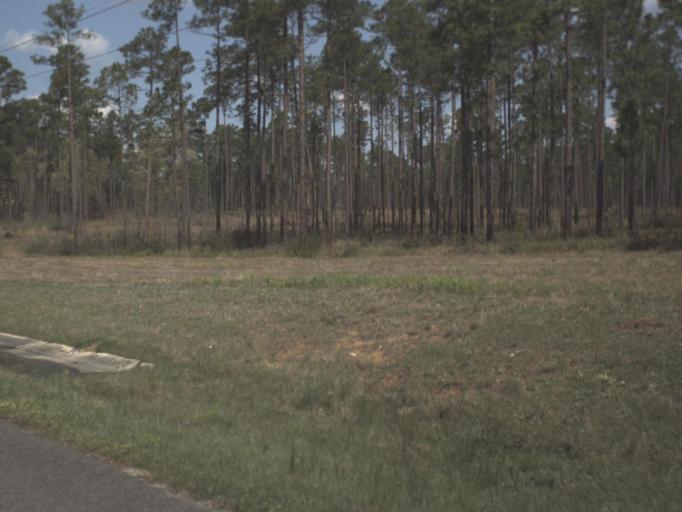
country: US
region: Florida
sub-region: Santa Rosa County
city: Point Baker
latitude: 30.8686
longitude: -86.9227
